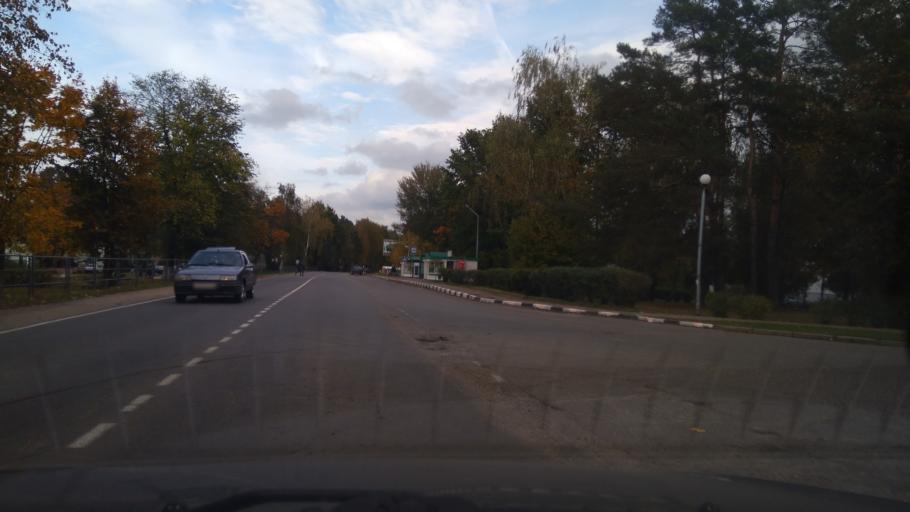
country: BY
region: Minsk
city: Svislach
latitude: 53.6454
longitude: 27.9156
